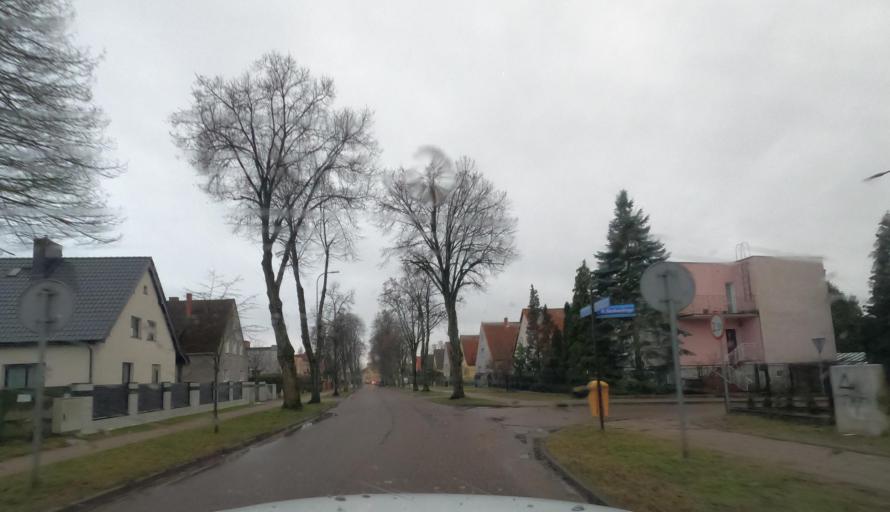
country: PL
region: West Pomeranian Voivodeship
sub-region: Powiat szczecinecki
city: Szczecinek
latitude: 53.7165
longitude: 16.6749
